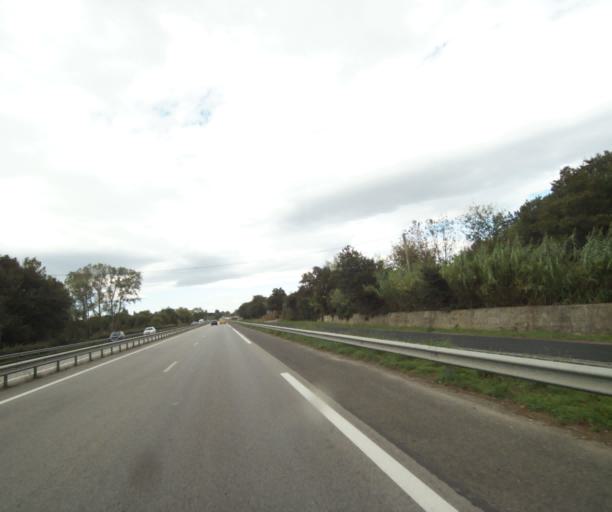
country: FR
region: Languedoc-Roussillon
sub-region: Departement des Pyrenees-Orientales
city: Argelers
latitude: 42.5697
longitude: 2.9998
